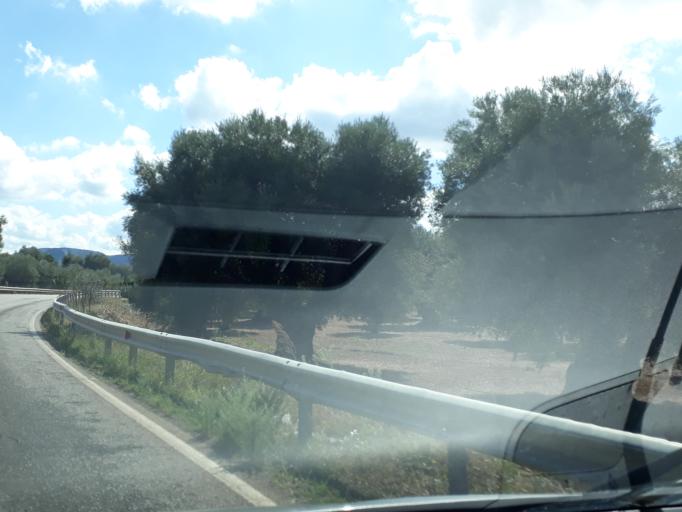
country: IT
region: Apulia
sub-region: Provincia di Brindisi
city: Fasano
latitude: 40.8210
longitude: 17.3761
